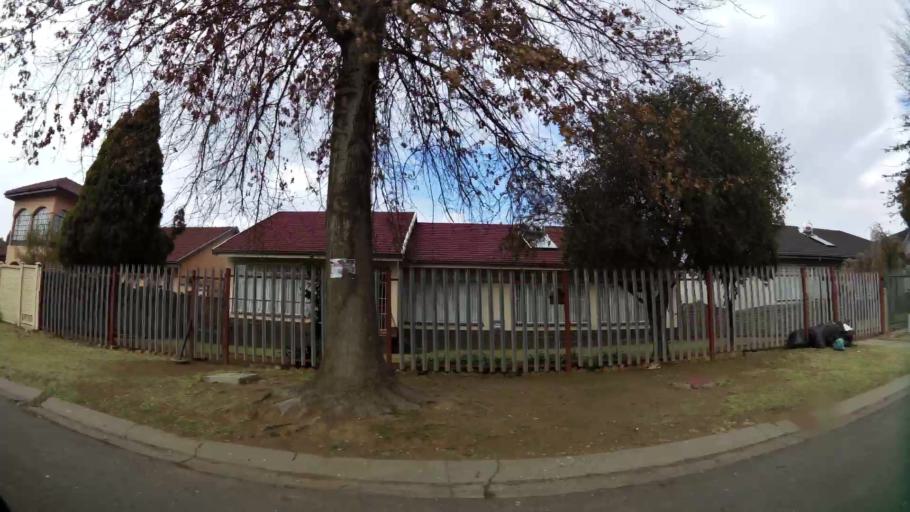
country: ZA
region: Gauteng
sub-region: Sedibeng District Municipality
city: Vanderbijlpark
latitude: -26.7143
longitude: 27.8587
